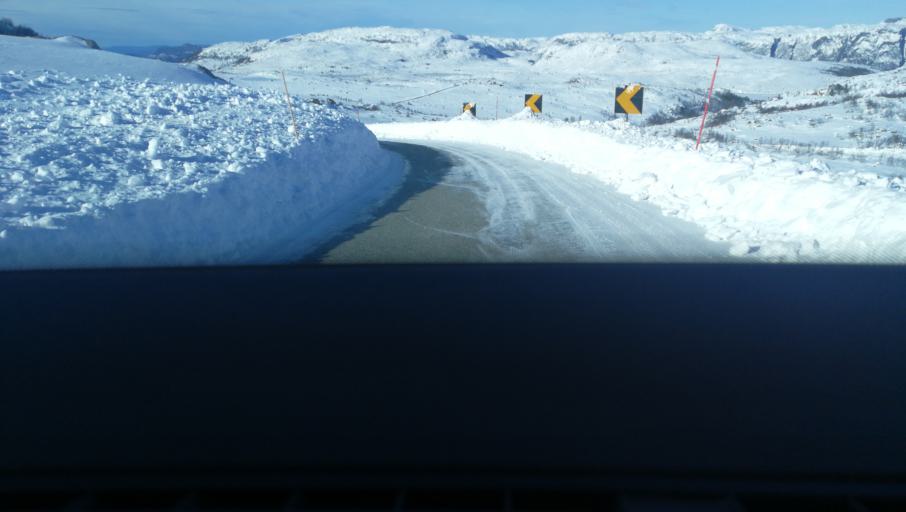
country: NO
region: Rogaland
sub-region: Hjelmeland
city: Hjelmelandsvagen
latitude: 59.1019
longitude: 6.3842
